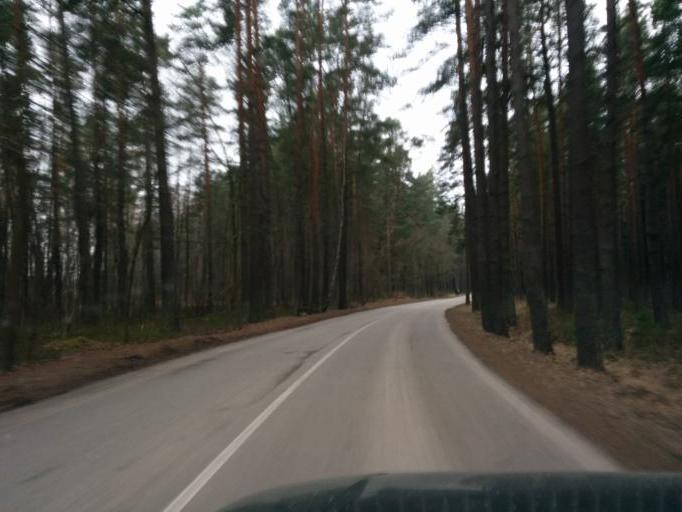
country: LV
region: Babite
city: Pinki
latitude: 56.9872
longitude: 23.9034
